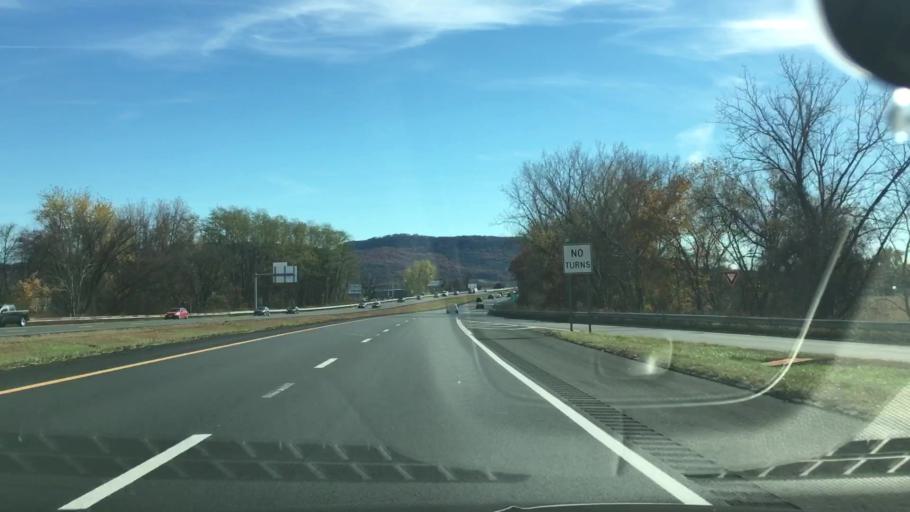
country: US
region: Massachusetts
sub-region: Hampshire County
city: Northampton
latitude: 42.3318
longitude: -72.6201
